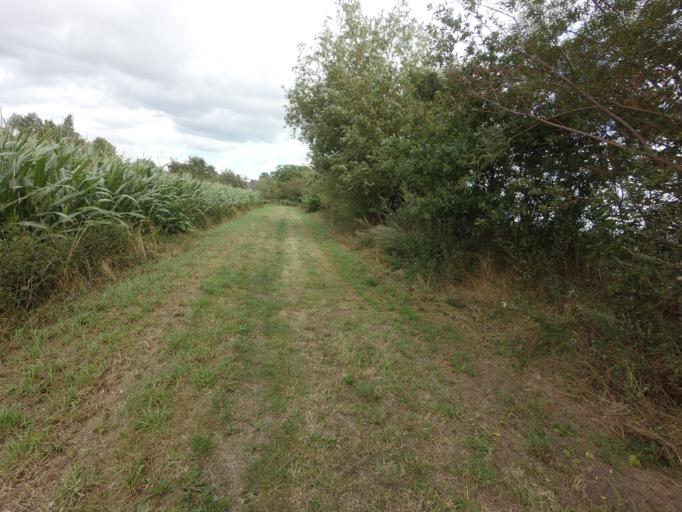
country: NL
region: Limburg
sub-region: Gemeente Maasgouw
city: Maasbracht
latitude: 51.1253
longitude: 5.8531
